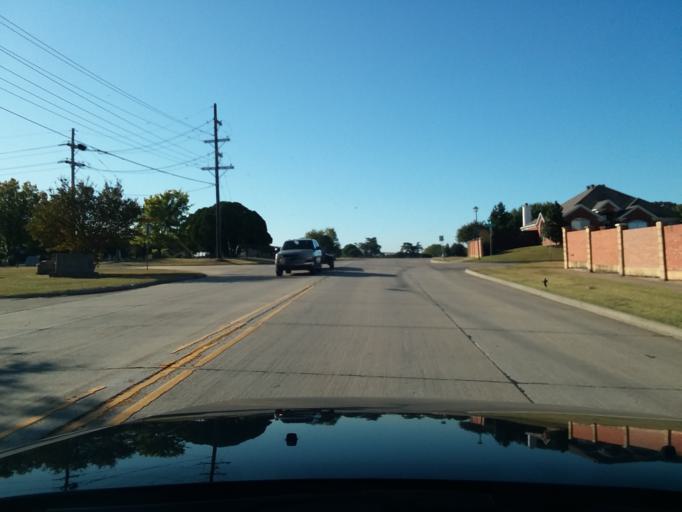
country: US
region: Texas
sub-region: Denton County
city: Highland Village
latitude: 33.0645
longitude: -97.0273
